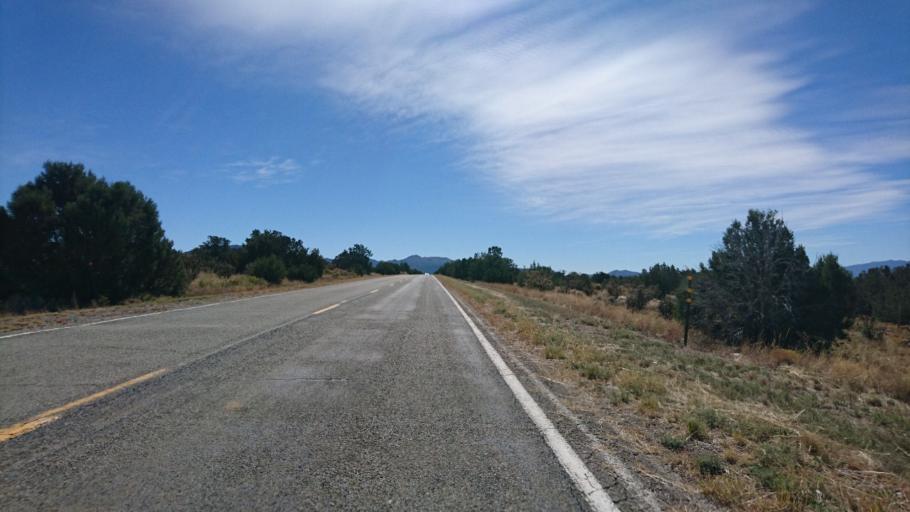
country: US
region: New Mexico
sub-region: Bernalillo County
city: Sandia Knolls
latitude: 35.3235
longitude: -106.2150
